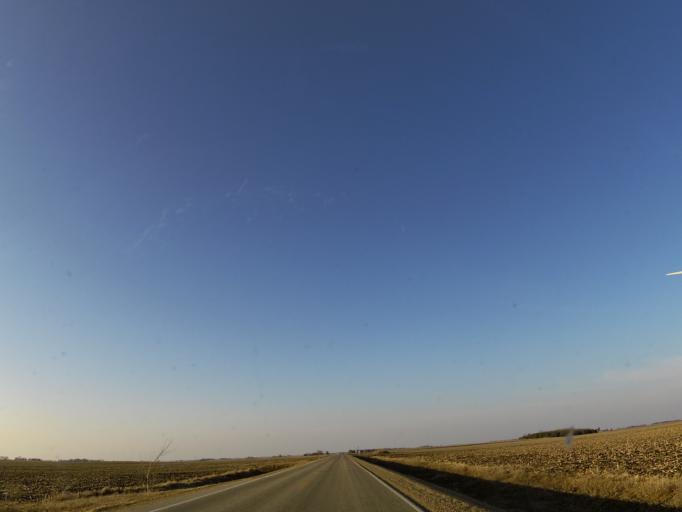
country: US
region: Iowa
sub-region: Worth County
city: Northwood
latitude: 43.4206
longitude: -93.1244
